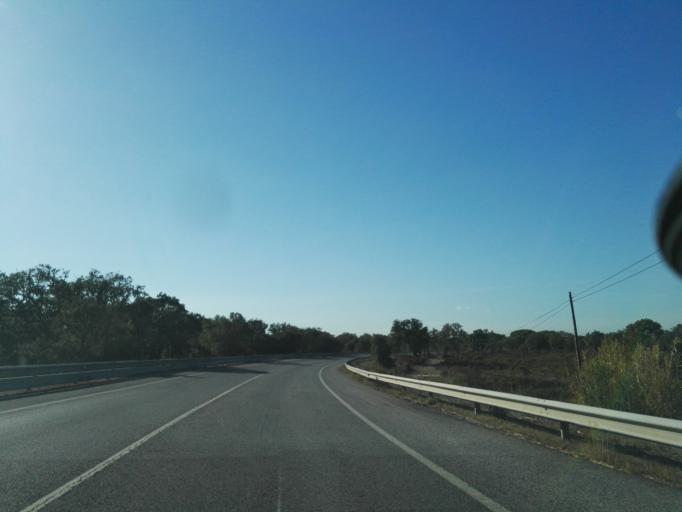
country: PT
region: Santarem
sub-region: Benavente
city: Poceirao
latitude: 38.8465
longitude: -8.7672
